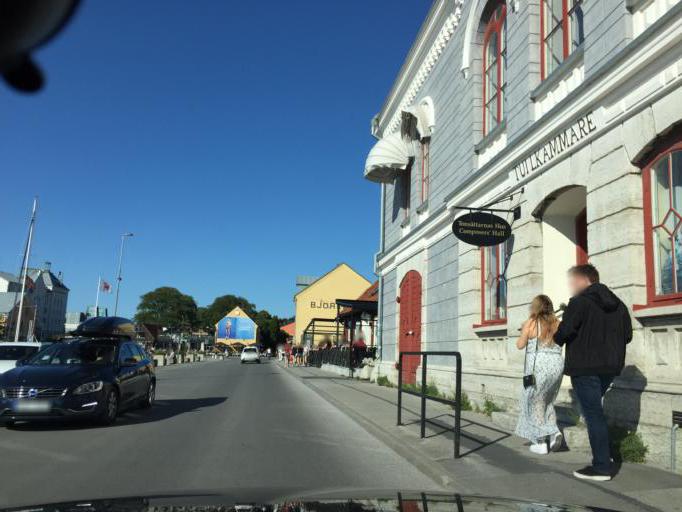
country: SE
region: Gotland
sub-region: Gotland
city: Visby
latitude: 57.6377
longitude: 18.2876
